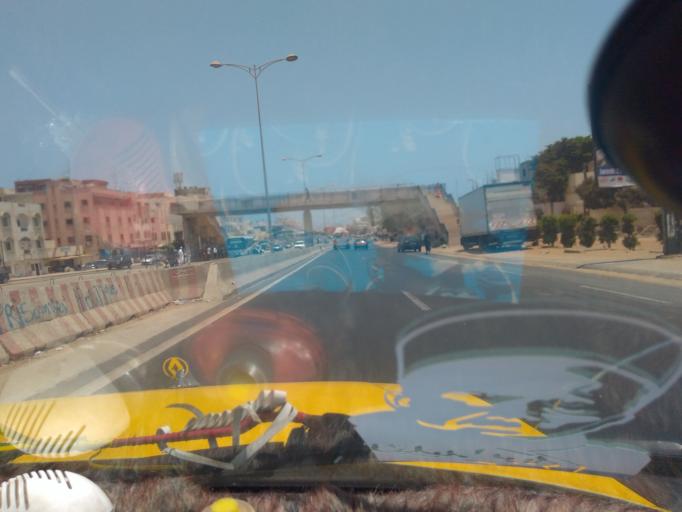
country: SN
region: Dakar
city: Grand Dakar
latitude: 14.7503
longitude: -17.4645
